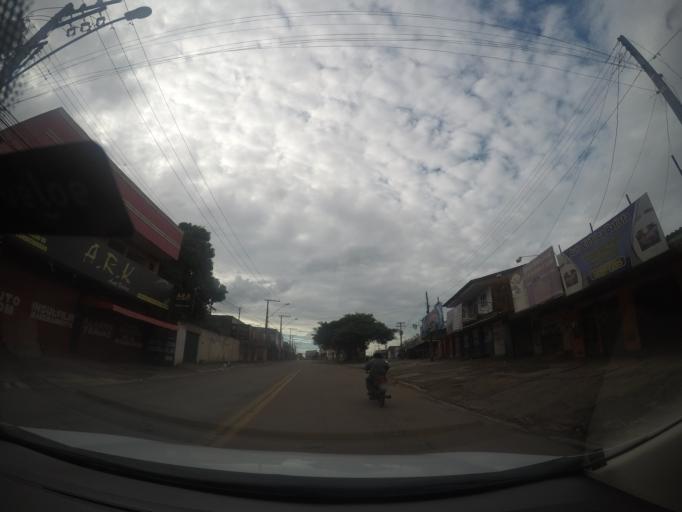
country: BR
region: Goias
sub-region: Goiania
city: Goiania
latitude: -16.6400
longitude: -49.3297
